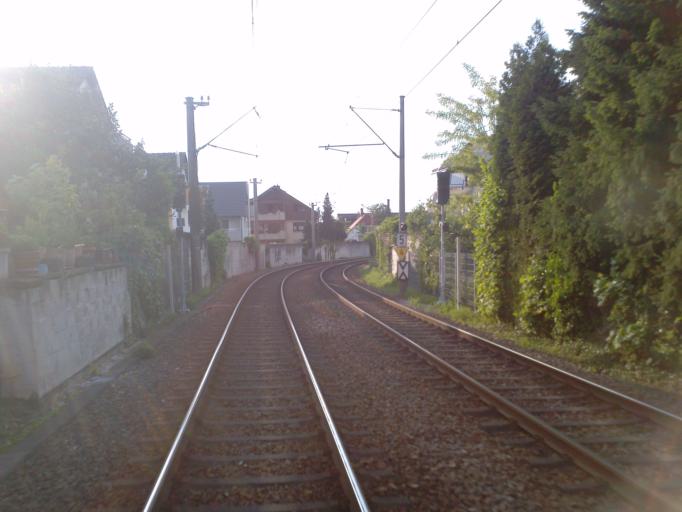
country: DE
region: Baden-Wuerttemberg
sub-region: Karlsruhe Region
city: Ettlingen
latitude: 48.9431
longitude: 8.4003
